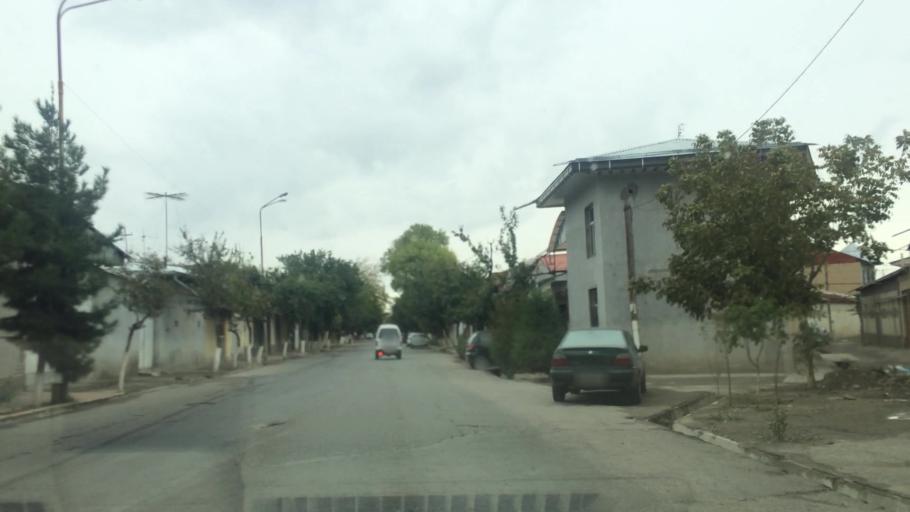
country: UZ
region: Samarqand
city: Samarqand
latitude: 39.6602
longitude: 66.9740
